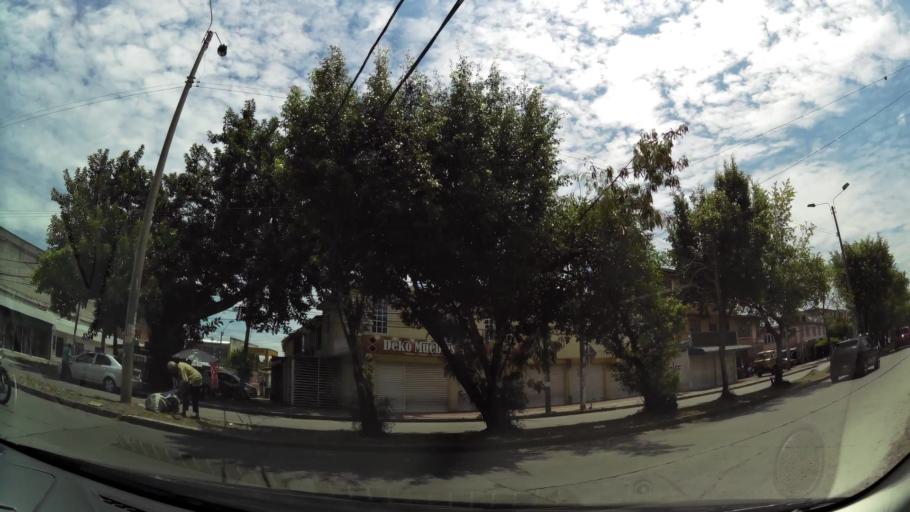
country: CO
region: Valle del Cauca
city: Cali
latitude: 3.4427
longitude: -76.4997
